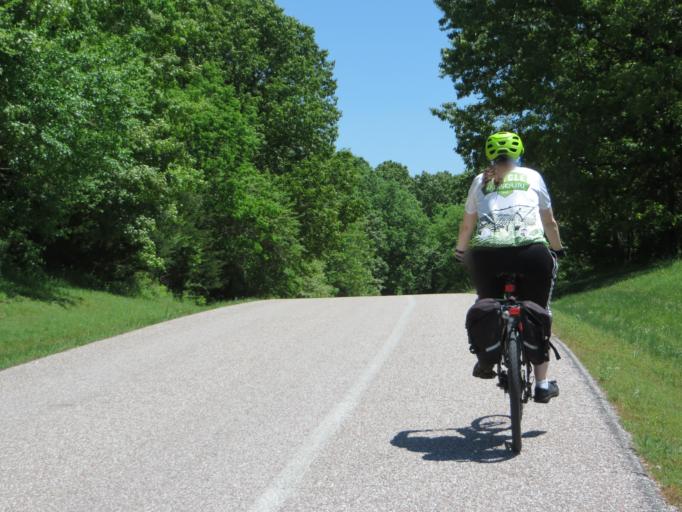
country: US
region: Missouri
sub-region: Greene County
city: Battlefield
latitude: 37.1108
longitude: -93.4002
